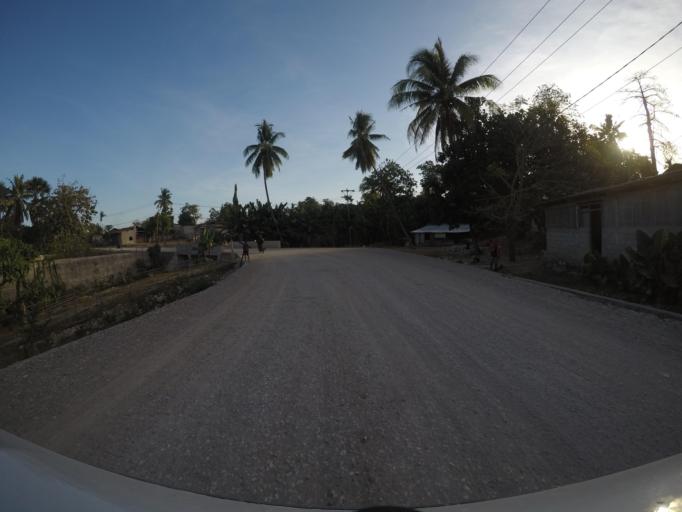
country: TL
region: Viqueque
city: Viqueque
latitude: -8.8467
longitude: 126.5127
